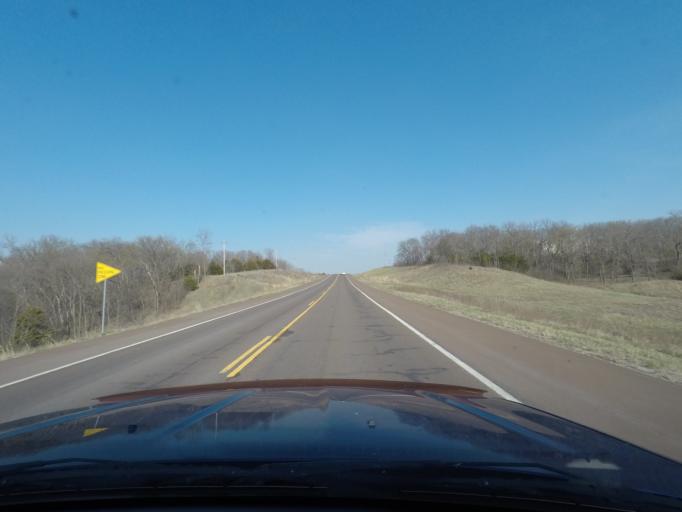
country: US
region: Kansas
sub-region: Douglas County
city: Lawrence
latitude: 39.0004
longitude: -95.3585
